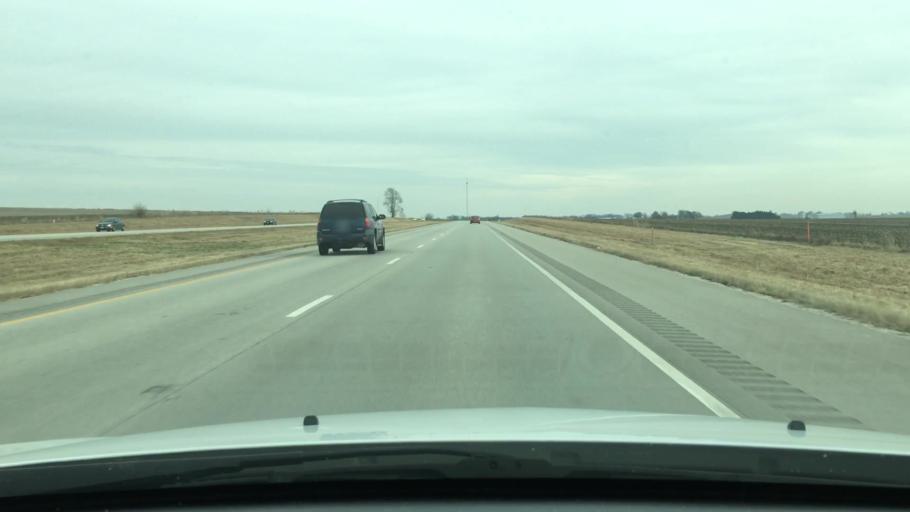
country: US
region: Illinois
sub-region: Morgan County
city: Jacksonville
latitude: 39.7380
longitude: -90.0995
